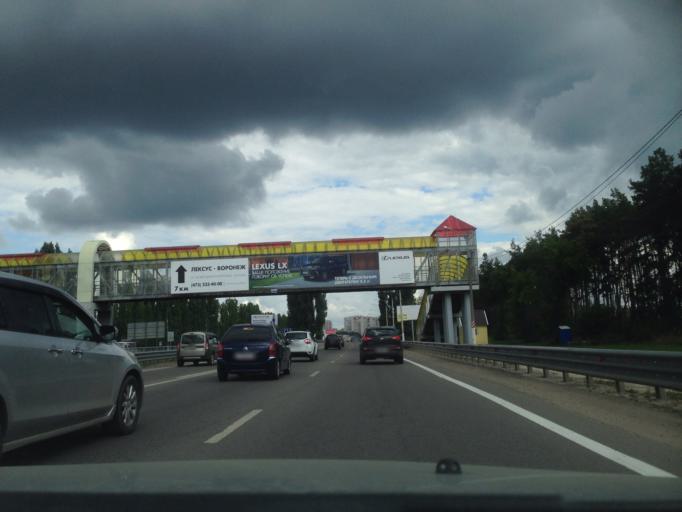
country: RU
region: Voronezj
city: Podgornoye
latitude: 51.7218
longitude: 39.1796
